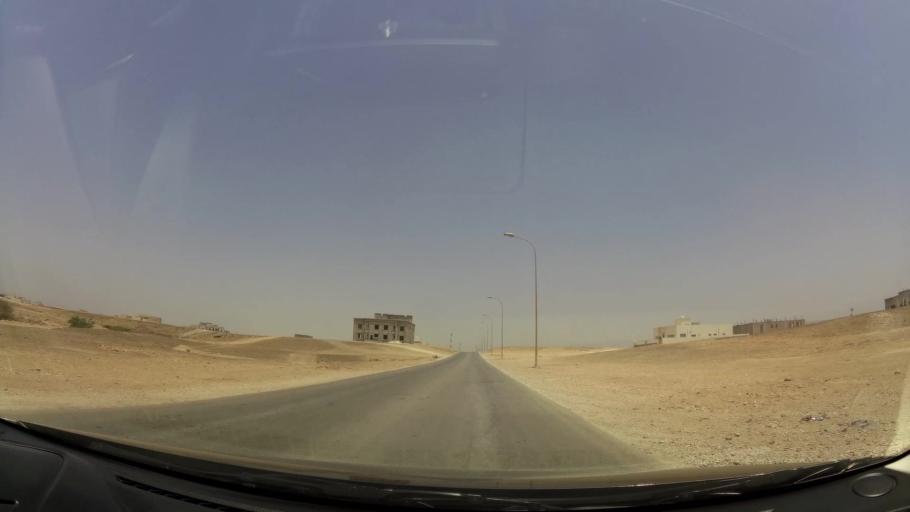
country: OM
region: Zufar
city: Salalah
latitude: 17.0917
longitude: 54.1956
